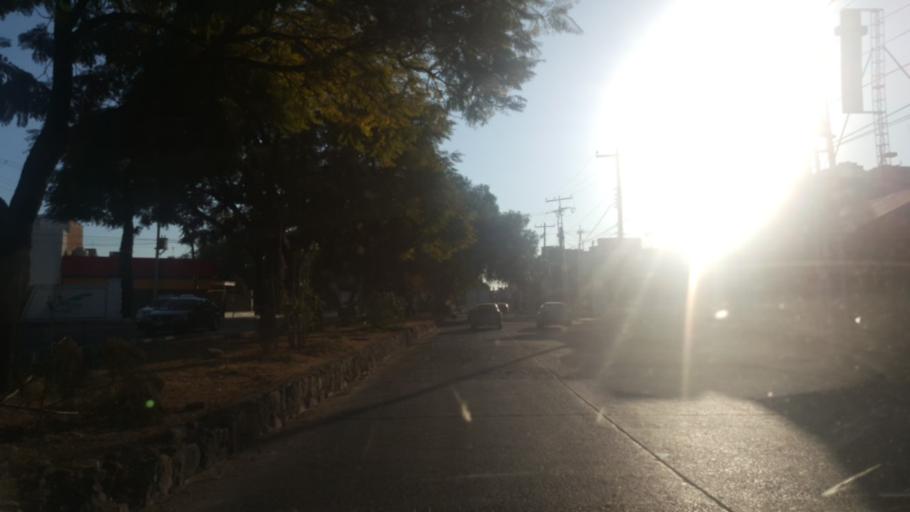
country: MX
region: Guanajuato
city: Leon
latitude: 21.1106
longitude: -101.6351
